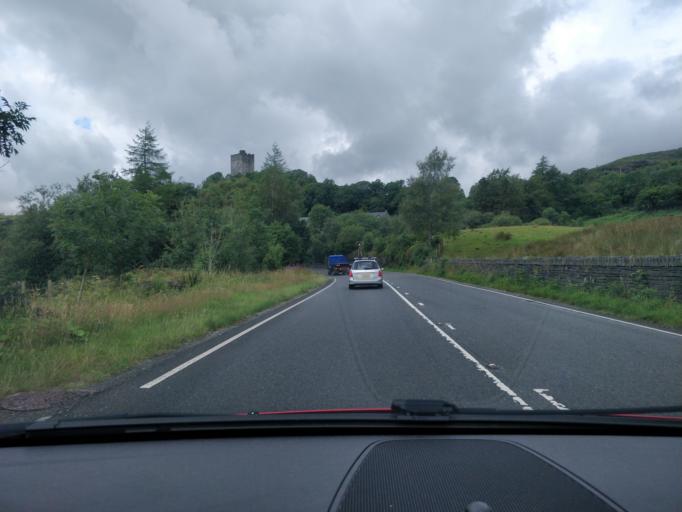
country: GB
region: Wales
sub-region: Gwynedd
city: Blaenau-Ffestiniog
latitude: 53.0535
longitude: -3.9027
